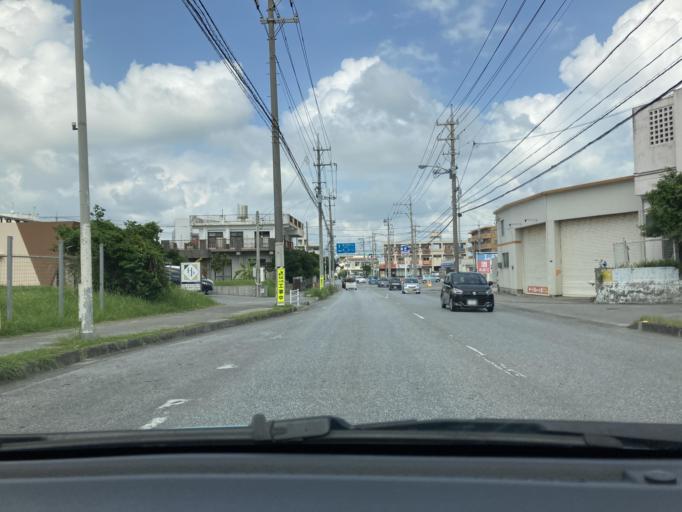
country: JP
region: Okinawa
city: Ginowan
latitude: 26.2534
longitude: 127.7734
